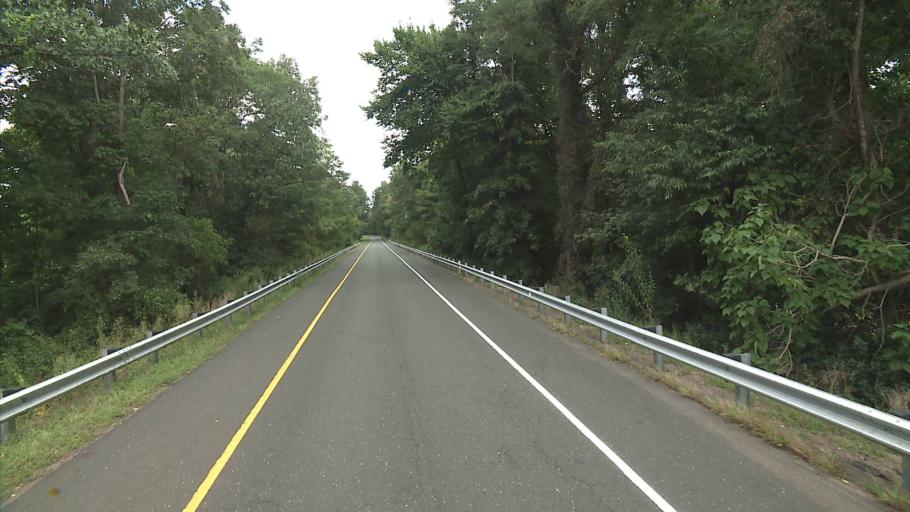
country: US
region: Connecticut
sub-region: Hartford County
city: Tariffville
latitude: 41.8905
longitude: -72.7487
